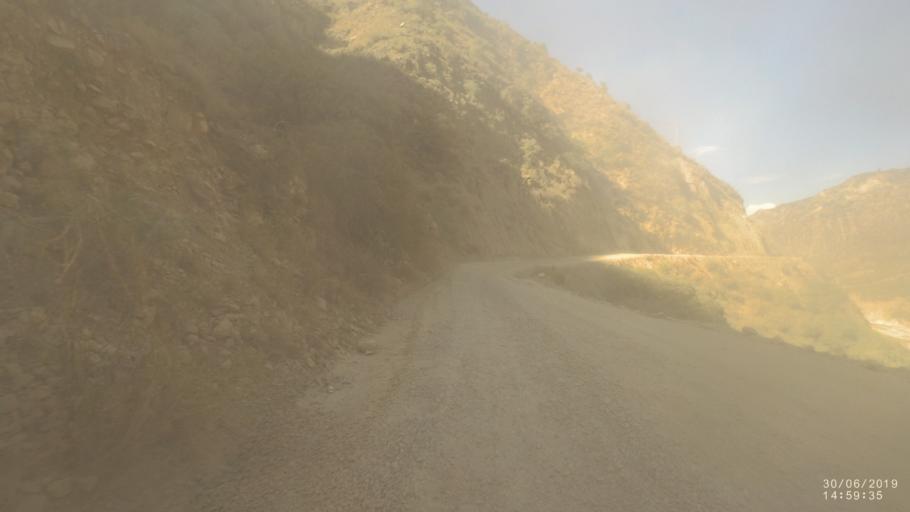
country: BO
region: Cochabamba
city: Irpa Irpa
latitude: -17.7366
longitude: -66.3446
